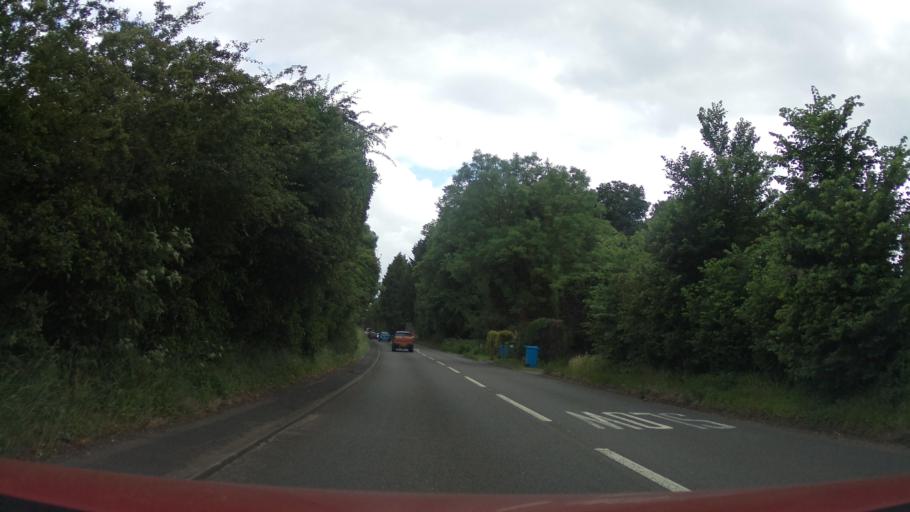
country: GB
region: England
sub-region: Dudley
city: Kingswinford
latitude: 52.4741
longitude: -2.1940
